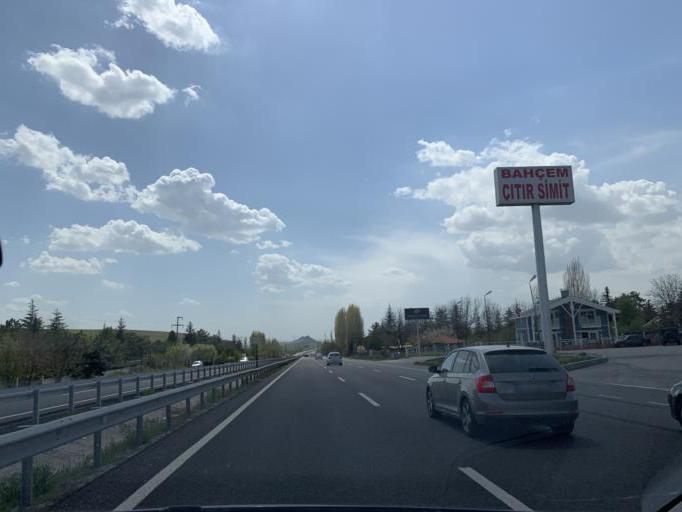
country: TR
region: Ankara
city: Etimesgut
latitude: 39.7965
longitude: 32.5339
